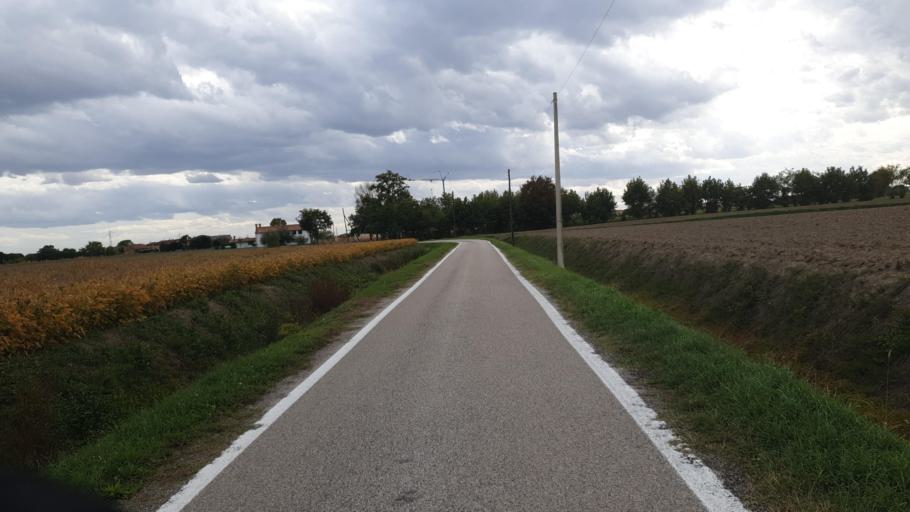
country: IT
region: Veneto
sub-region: Provincia di Padova
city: Polverara
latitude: 45.2835
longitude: 11.9649
